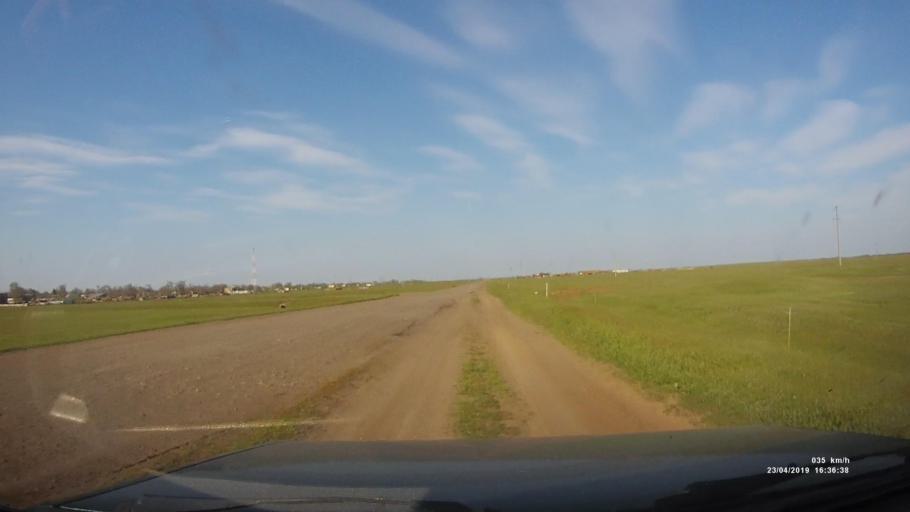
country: RU
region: Kalmykiya
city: Priyutnoye
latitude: 46.3302
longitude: 43.1411
